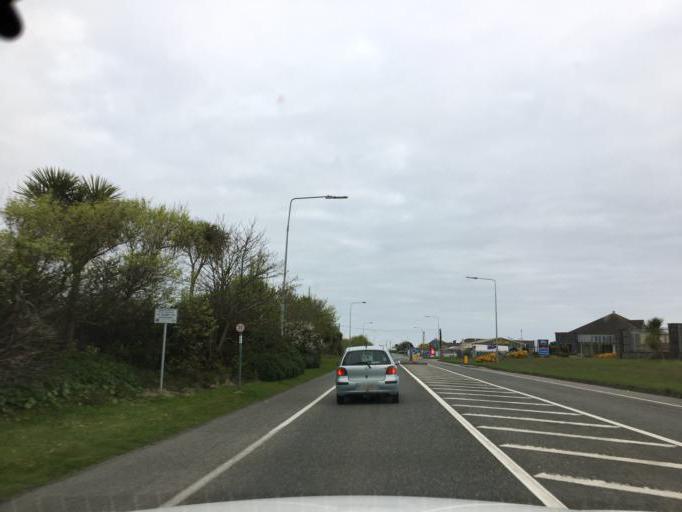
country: IE
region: Leinster
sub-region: Loch Garman
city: Ballygerry
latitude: 52.2455
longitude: -6.3460
